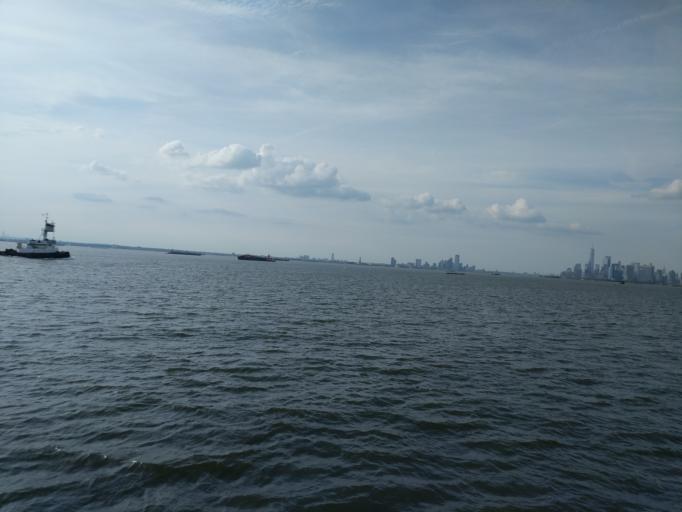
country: US
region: New York
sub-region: Kings County
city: Bensonhurst
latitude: 40.6469
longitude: -74.0345
